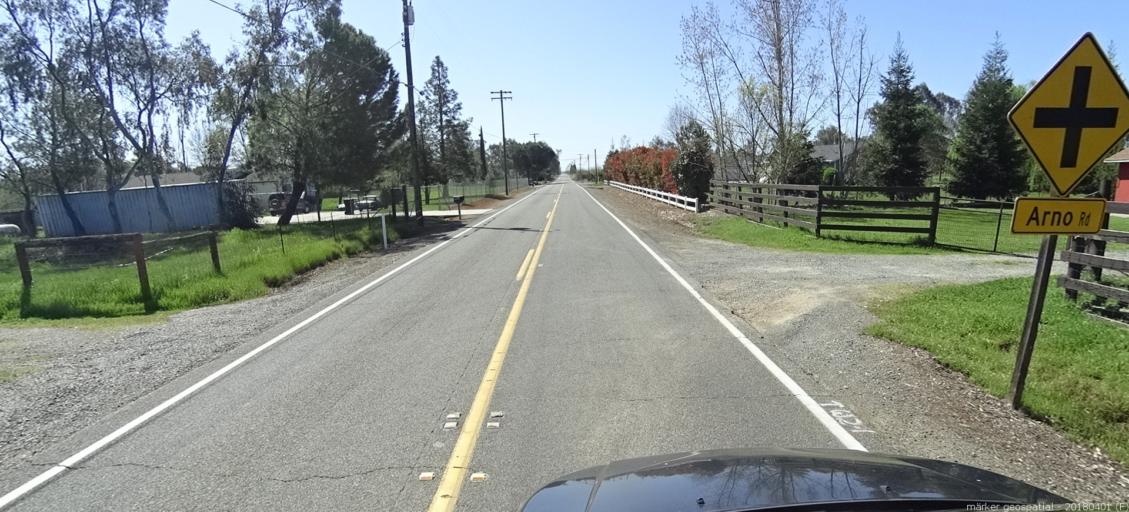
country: US
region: California
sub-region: Sacramento County
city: Herald
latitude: 38.3445
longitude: -121.2238
